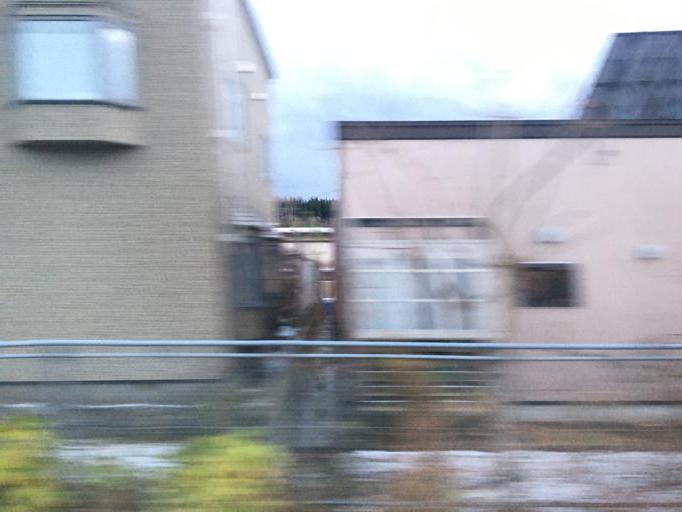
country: JP
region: Aomori
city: Aomori Shi
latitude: 40.8241
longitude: 140.6604
